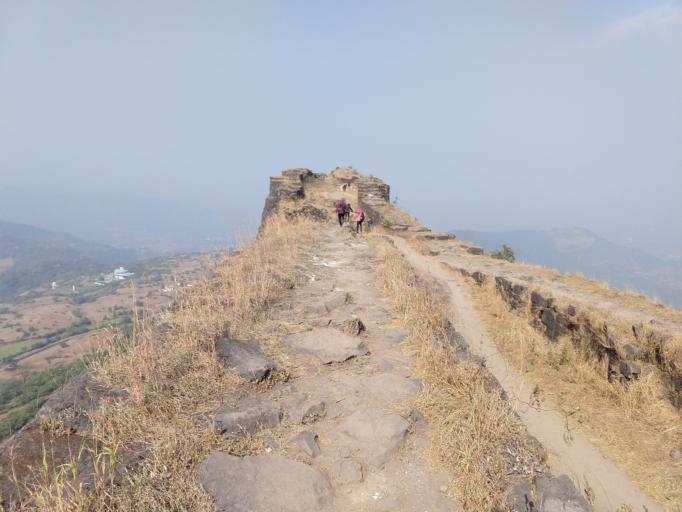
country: IN
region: Maharashtra
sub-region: Pune Division
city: Lonavla
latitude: 18.7130
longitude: 73.4711
